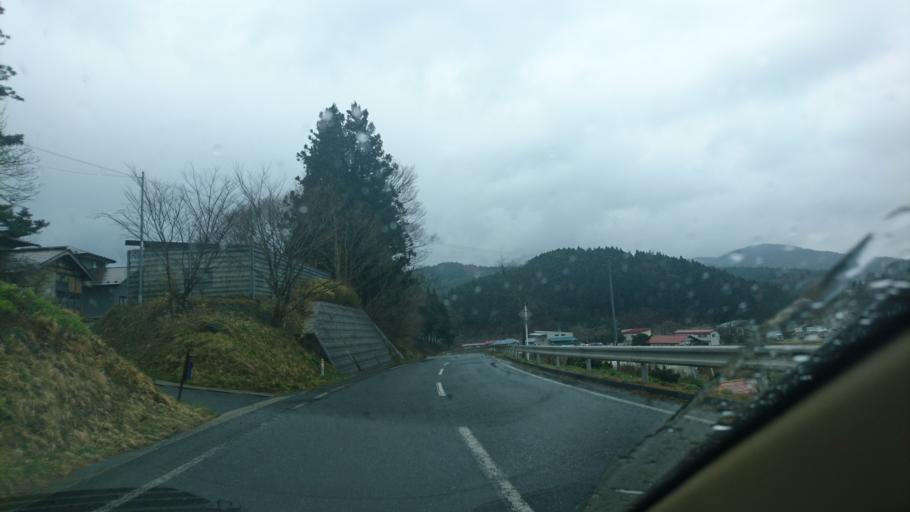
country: JP
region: Iwate
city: Ofunato
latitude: 38.9407
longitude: 141.4613
